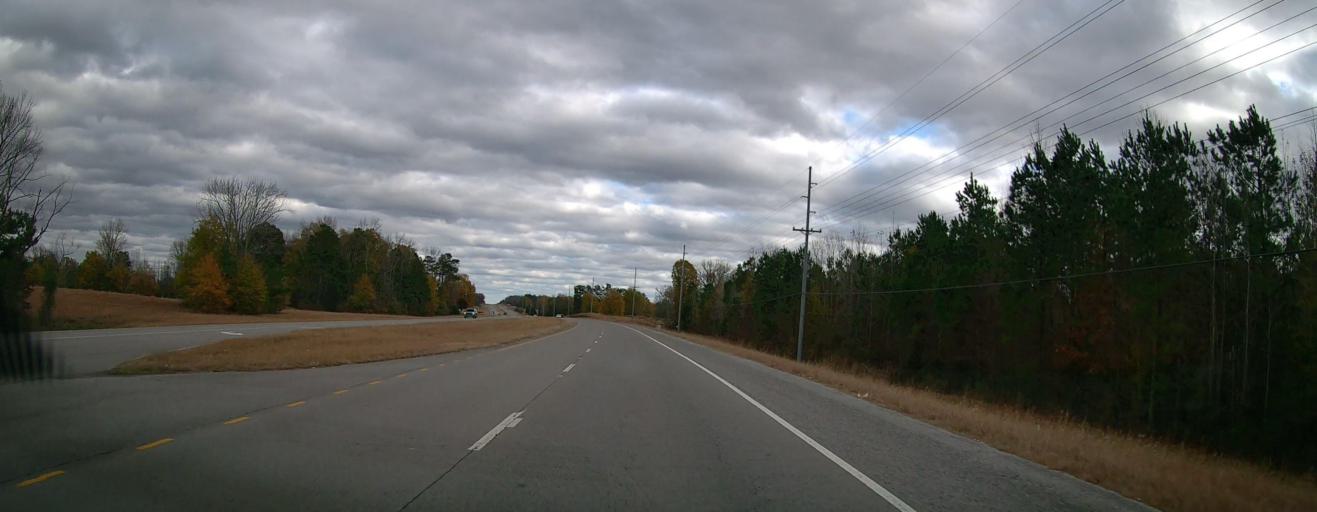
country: US
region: Alabama
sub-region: Lawrence County
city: Town Creek
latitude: 34.5751
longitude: -87.4009
